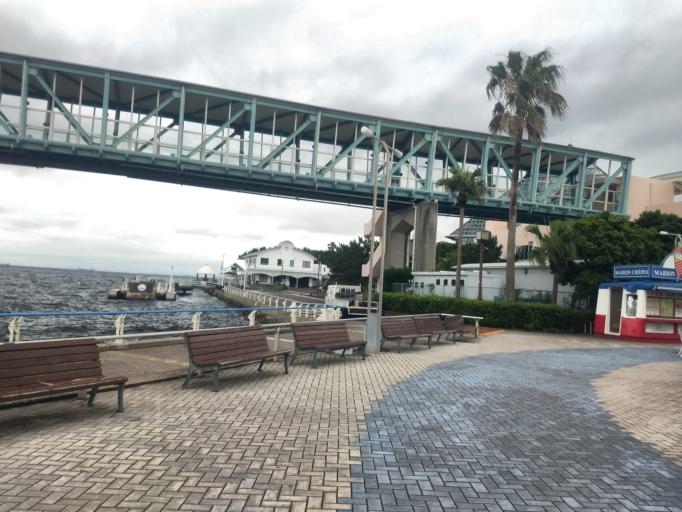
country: JP
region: Kanagawa
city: Yokosuka
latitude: 35.3385
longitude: 139.6458
